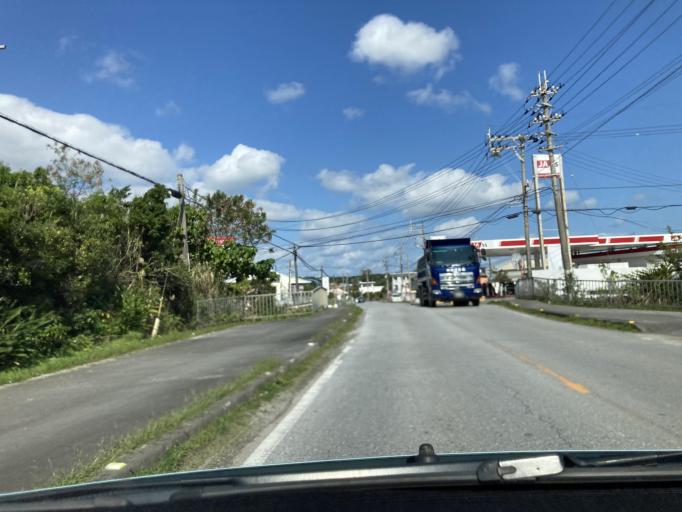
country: JP
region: Okinawa
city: Nago
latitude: 26.6154
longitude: 128.0003
